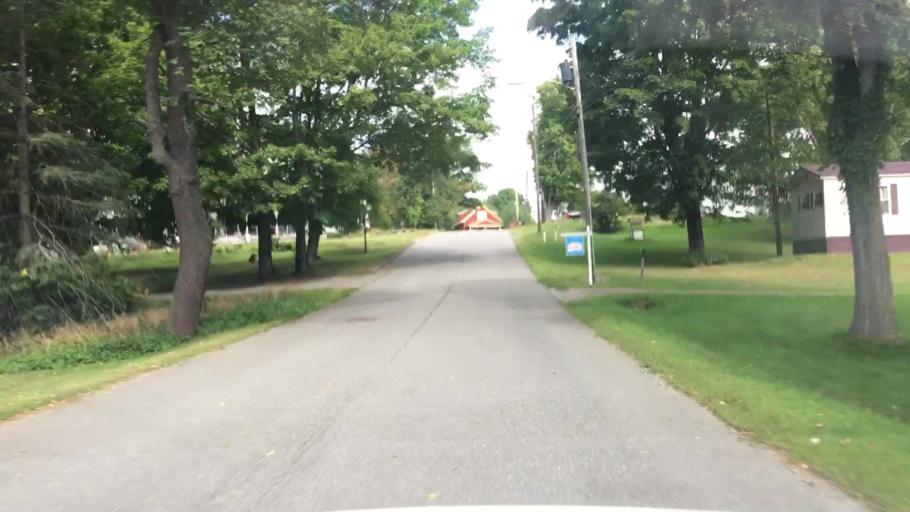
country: US
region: Maine
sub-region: Piscataquis County
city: Dover-Foxcroft
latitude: 45.1898
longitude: -69.2229
